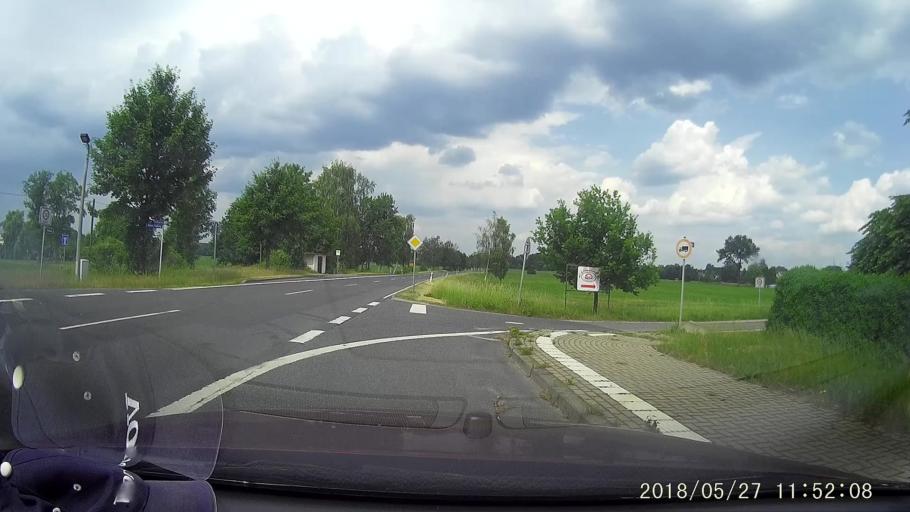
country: DE
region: Saxony
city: Quitzdorf
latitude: 51.2972
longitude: 14.7772
